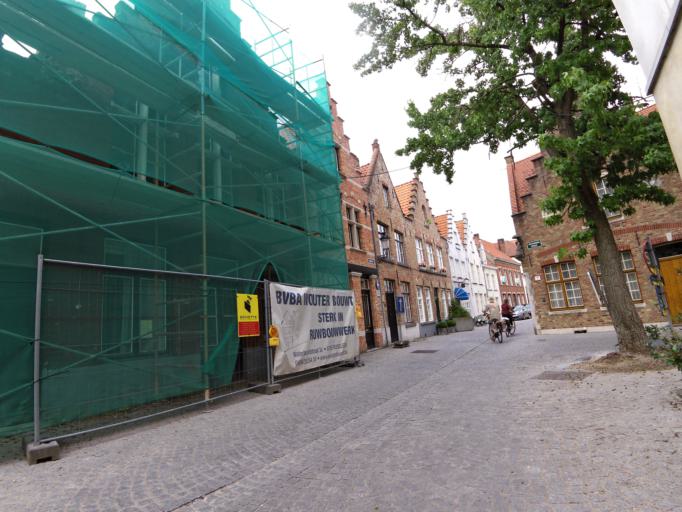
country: BE
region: Flanders
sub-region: Provincie West-Vlaanderen
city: Brugge
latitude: 51.2086
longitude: 3.2190
